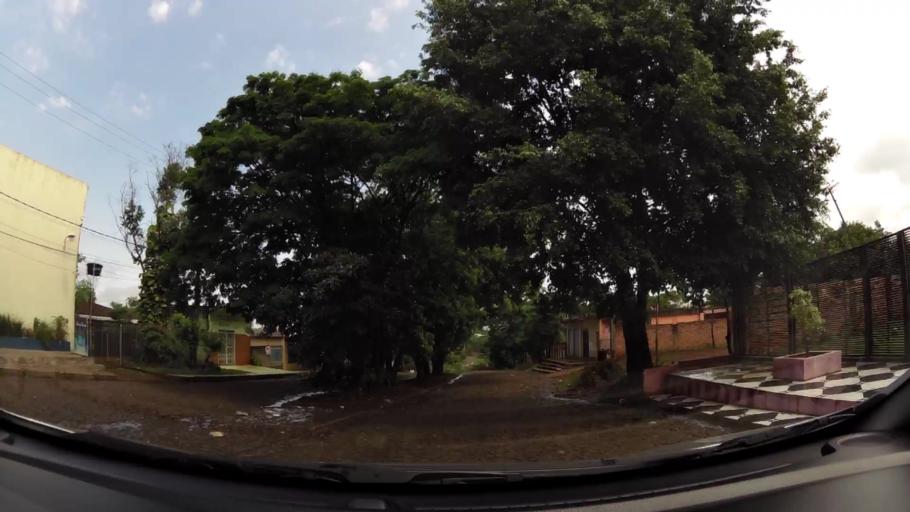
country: PY
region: Alto Parana
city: Ciudad del Este
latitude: -25.5058
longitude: -54.6724
